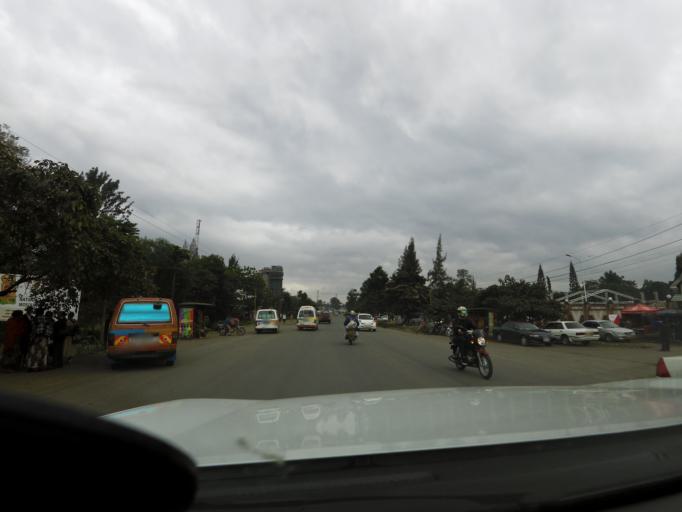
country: TZ
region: Arusha
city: Arusha
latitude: -3.3630
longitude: 36.6761
